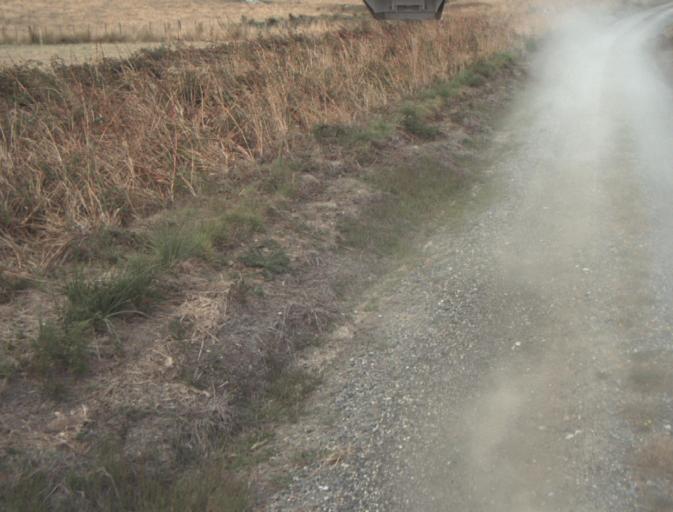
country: AU
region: Tasmania
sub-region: Launceston
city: Mayfield
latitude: -41.2131
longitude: 147.1082
